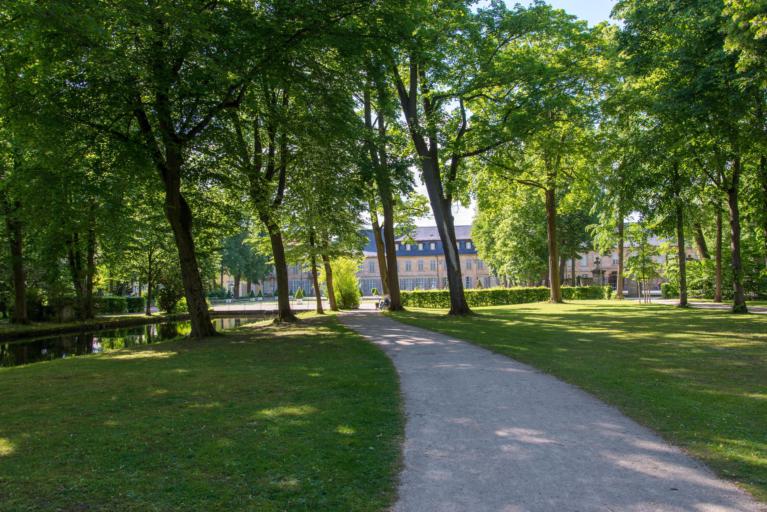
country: DE
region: Bavaria
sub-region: Upper Franconia
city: Bayreuth
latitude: 49.9410
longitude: 11.5789
